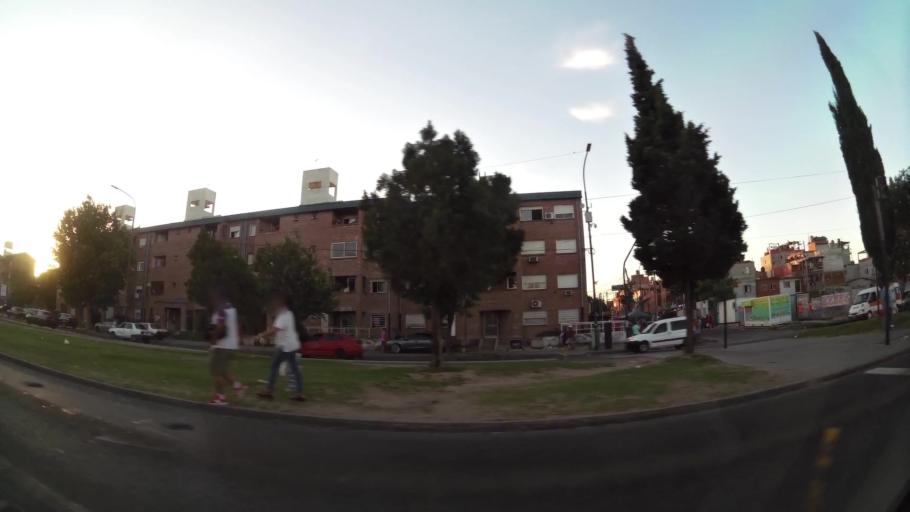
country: AR
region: Buenos Aires F.D.
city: Villa Lugano
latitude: -34.6781
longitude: -58.4646
